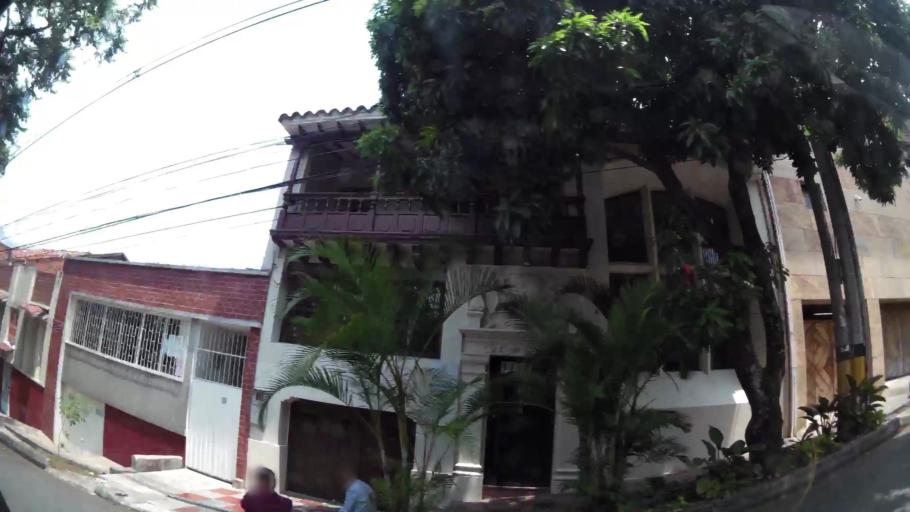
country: CO
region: Antioquia
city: Medellin
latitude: 6.2595
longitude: -75.5633
